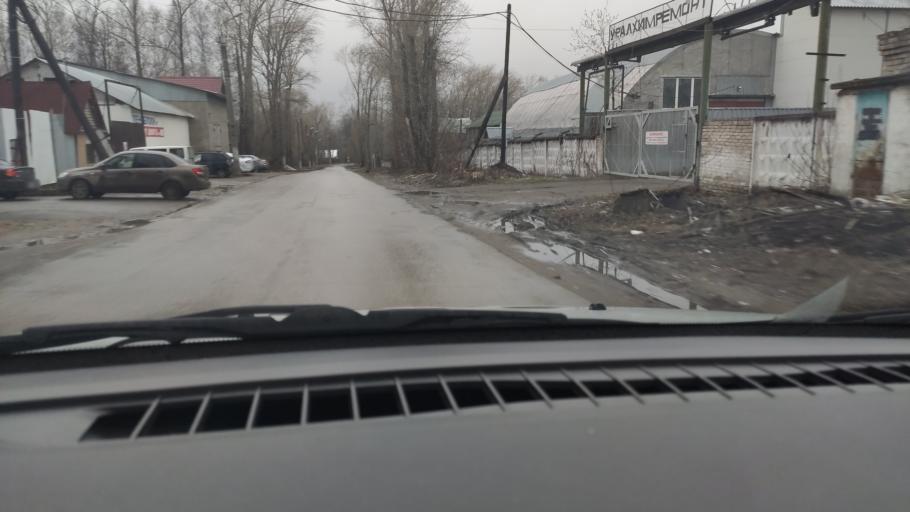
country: RU
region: Perm
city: Perm
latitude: 58.0970
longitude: 56.3701
